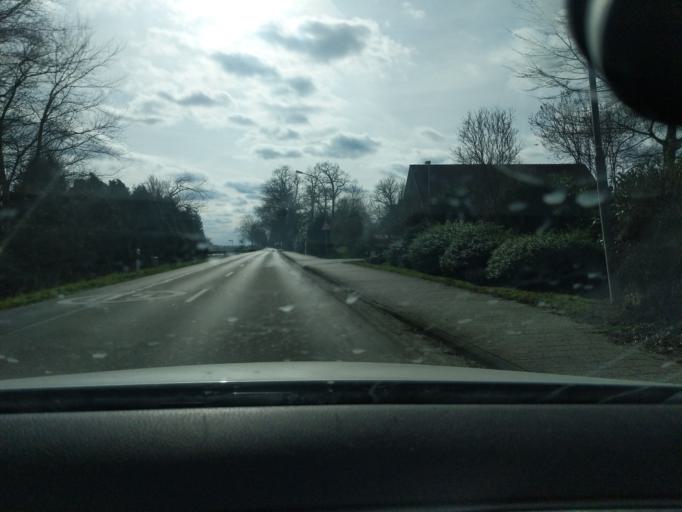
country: DE
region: Lower Saxony
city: Drochtersen
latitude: 53.6951
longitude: 9.4078
